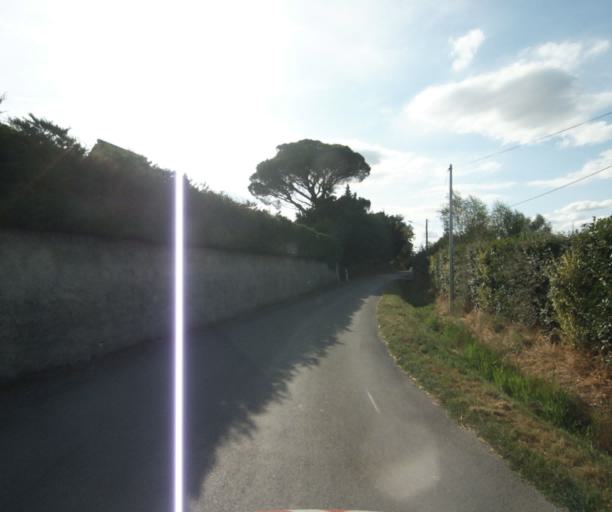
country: FR
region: Midi-Pyrenees
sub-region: Departement de la Haute-Garonne
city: Revel
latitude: 43.5033
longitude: 1.9964
